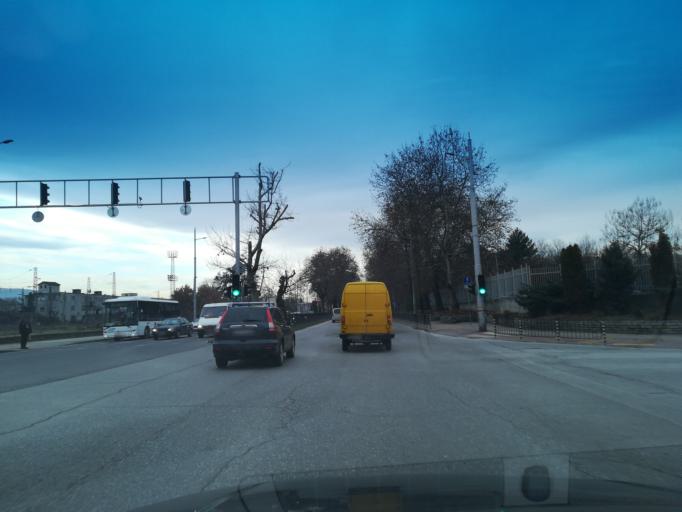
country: BG
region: Plovdiv
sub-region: Obshtina Plovdiv
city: Plovdiv
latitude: 42.1338
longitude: 24.7347
